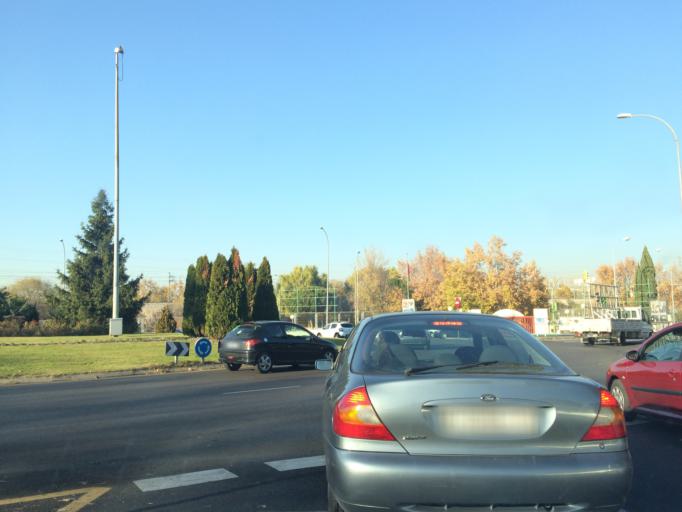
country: ES
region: Madrid
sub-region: Provincia de Madrid
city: Alcorcon
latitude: 40.3579
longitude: -3.8112
